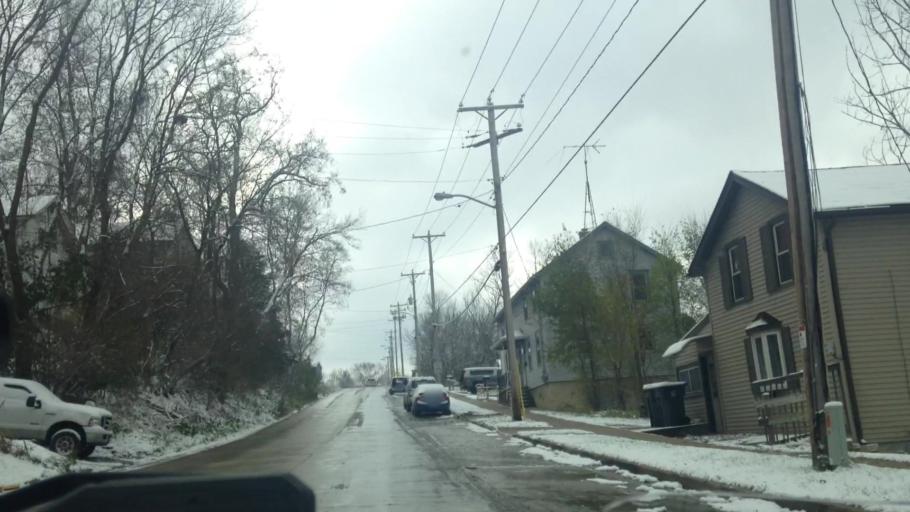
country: US
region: Wisconsin
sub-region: Dodge County
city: Mayville
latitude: 43.4956
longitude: -88.5420
